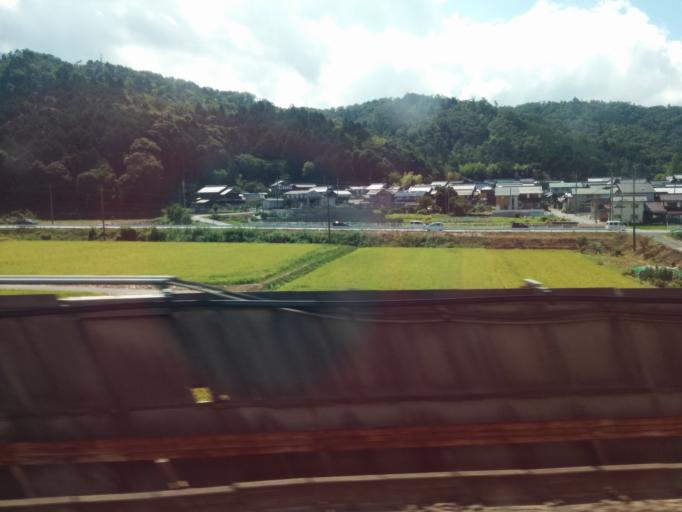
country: JP
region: Shiga Prefecture
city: Nagahama
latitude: 35.3519
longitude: 136.3112
